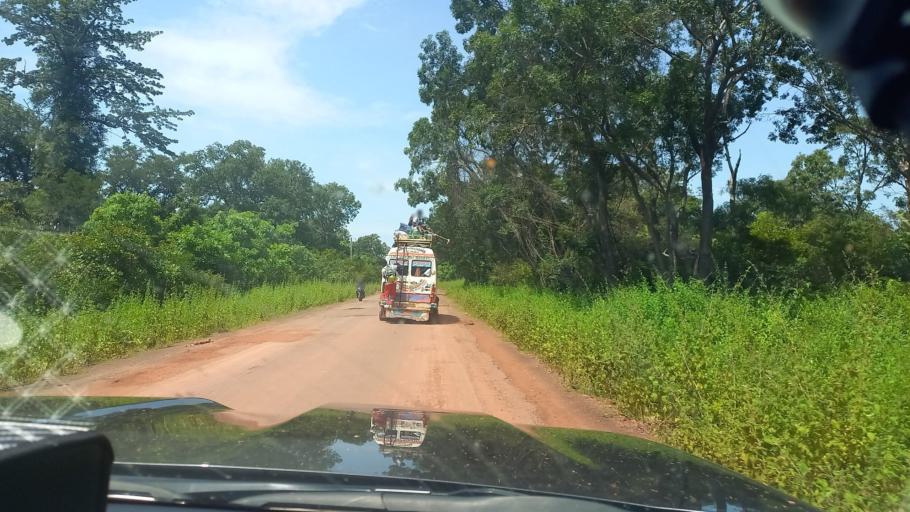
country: SN
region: Kolda
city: Marsassoum
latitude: 12.8574
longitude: -16.1056
